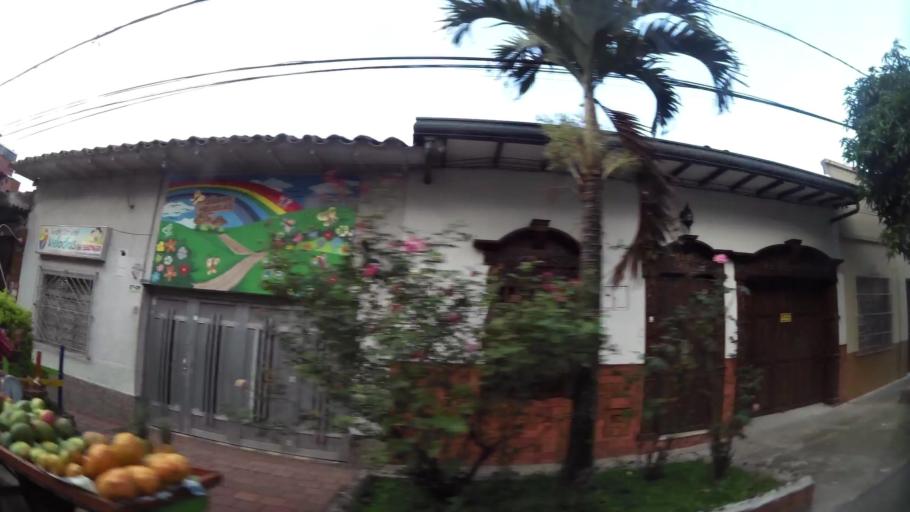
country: CO
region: Antioquia
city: Envigado
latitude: 6.1677
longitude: -75.5843
